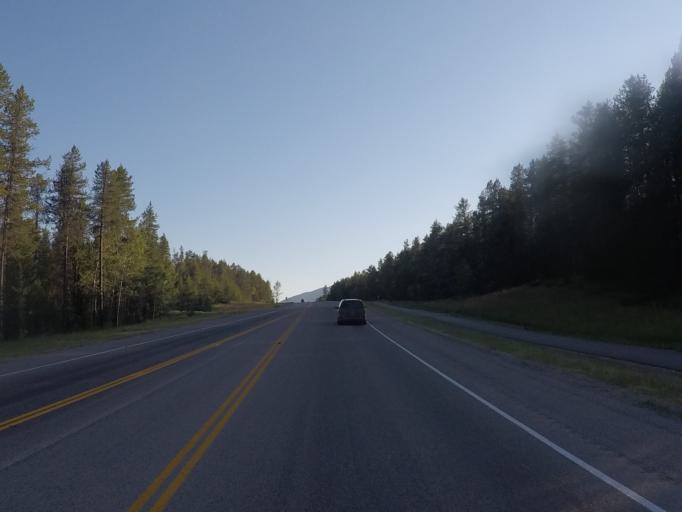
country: US
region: Montana
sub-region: Flathead County
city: Columbia Falls
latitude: 48.4609
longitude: -114.0047
